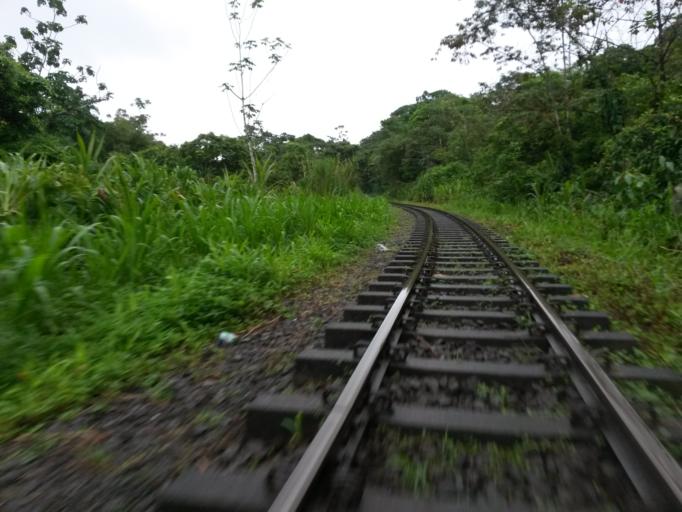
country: CO
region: Valle del Cauca
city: Buenaventura
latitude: 3.8430
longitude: -76.9047
